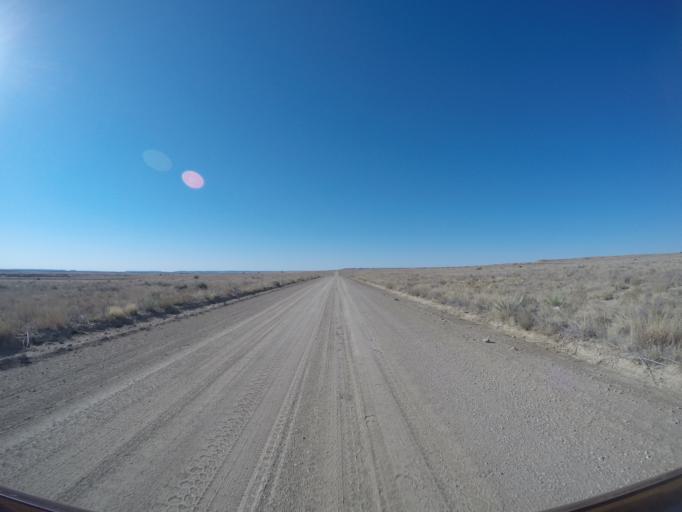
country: US
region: Colorado
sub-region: Otero County
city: La Junta
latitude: 37.7891
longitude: -103.5254
